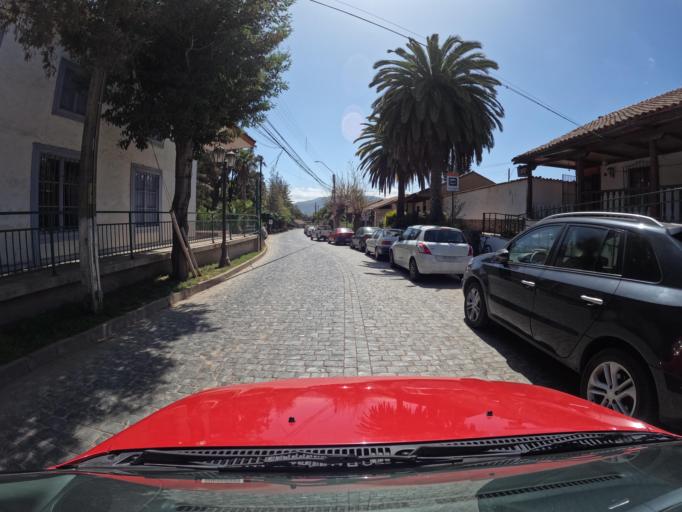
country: CL
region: O'Higgins
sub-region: Provincia de Colchagua
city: Santa Cruz
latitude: -34.7286
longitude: -71.6441
